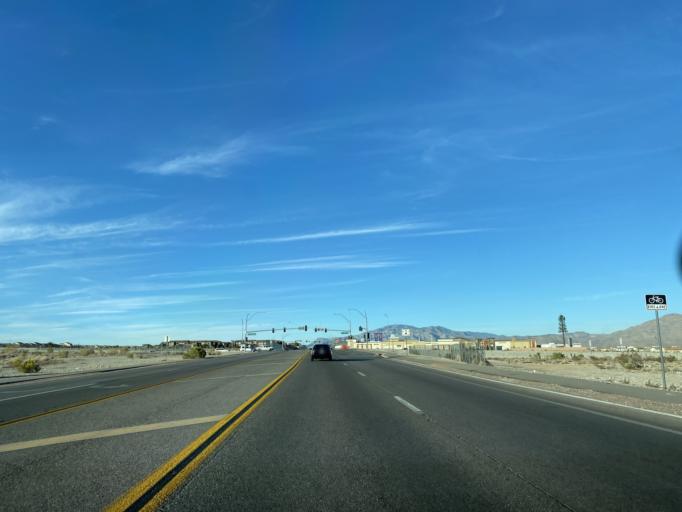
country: US
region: Nevada
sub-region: Clark County
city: Summerlin South
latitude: 36.2790
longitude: -115.3150
